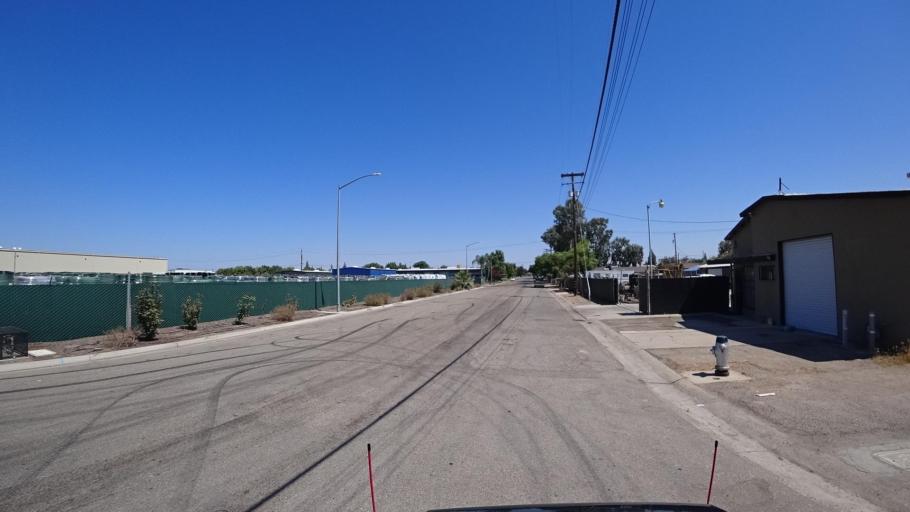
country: US
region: California
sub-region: Fresno County
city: Fresno
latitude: 36.7622
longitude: -119.7409
